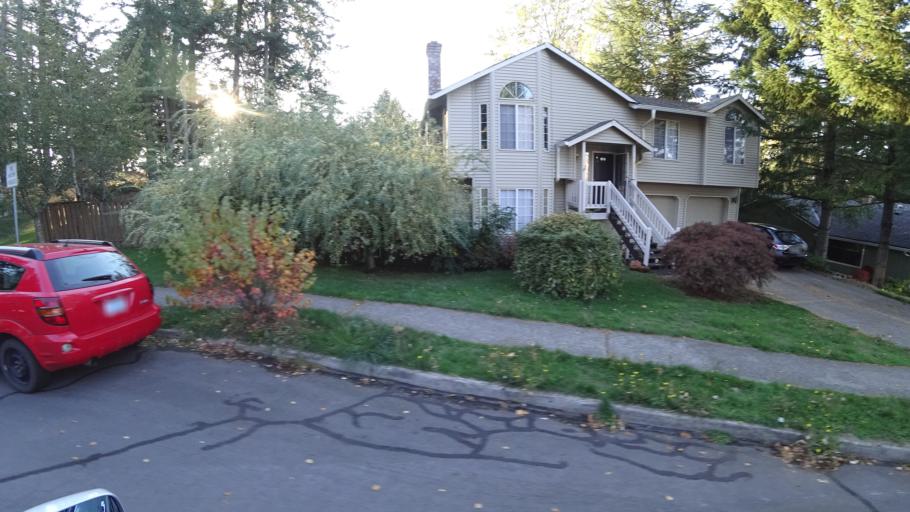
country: US
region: Oregon
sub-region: Multnomah County
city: Gresham
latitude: 45.4904
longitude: -122.4434
